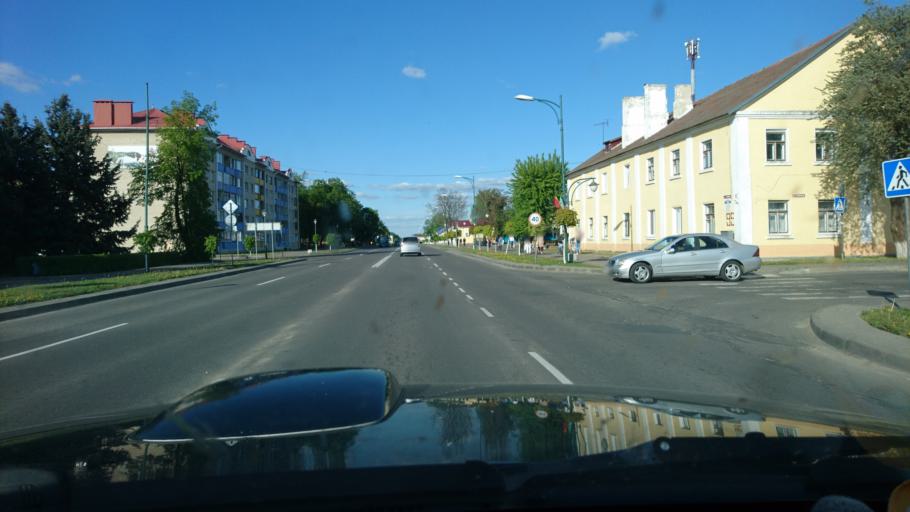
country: BY
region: Brest
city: Byaroza
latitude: 52.5293
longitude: 24.9746
